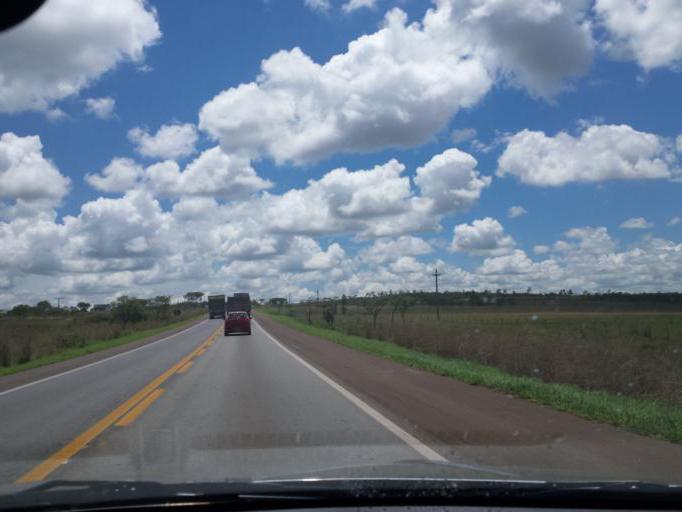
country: BR
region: Goias
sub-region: Cristalina
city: Cristalina
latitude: -16.7255
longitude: -47.6394
